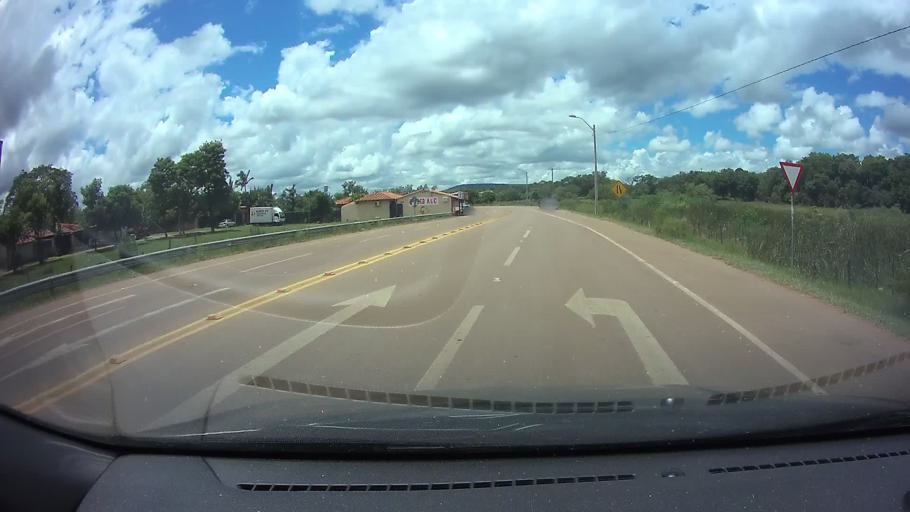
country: PY
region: Paraguari
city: La Colmena
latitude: -25.8926
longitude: -56.8441
